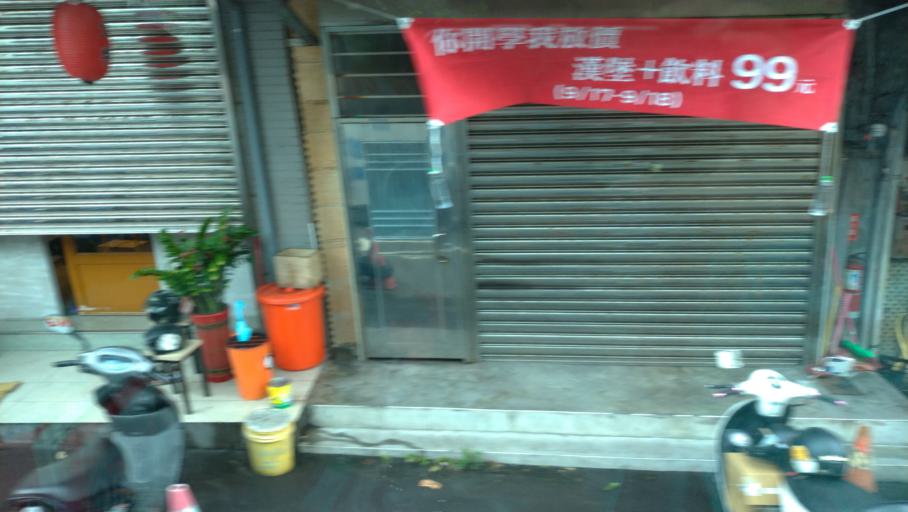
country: TW
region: Taiwan
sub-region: Keelung
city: Keelung
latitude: 25.1511
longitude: 121.7727
